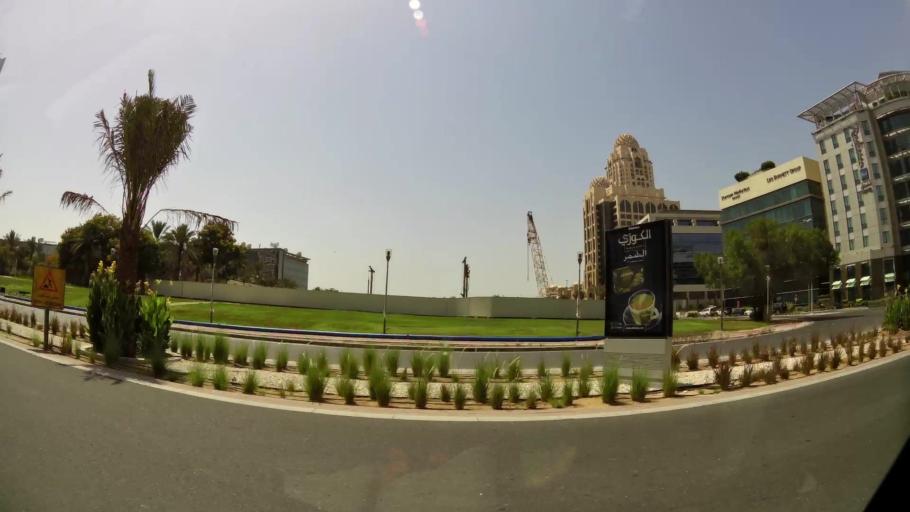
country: AE
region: Dubai
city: Dubai
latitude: 25.0929
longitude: 55.1550
